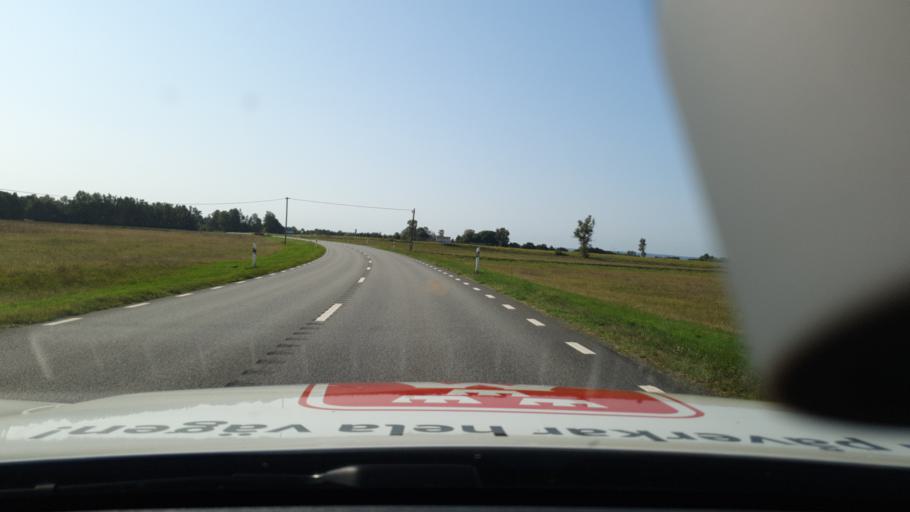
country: SE
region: Skane
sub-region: Kristianstads Kommun
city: Ahus
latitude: 55.9132
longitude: 14.2692
